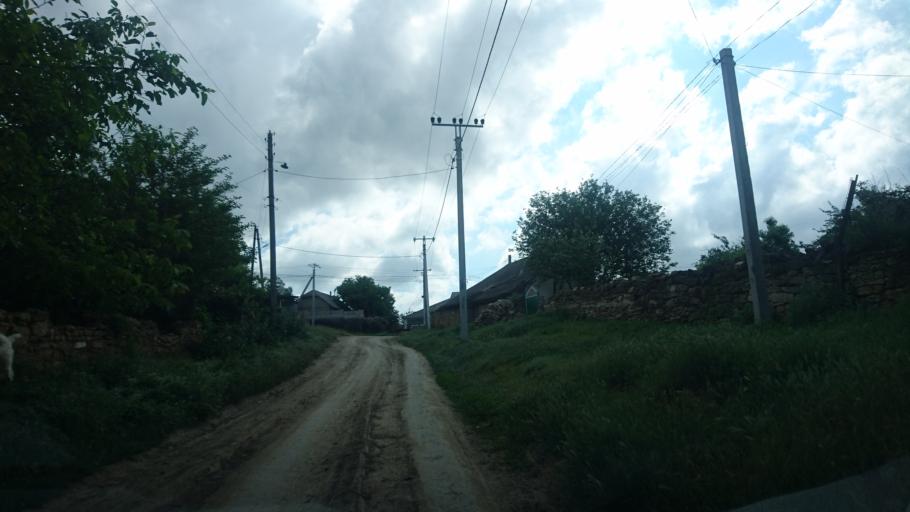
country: MD
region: Telenesti
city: Cocieri
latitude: 47.3611
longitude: 29.1023
